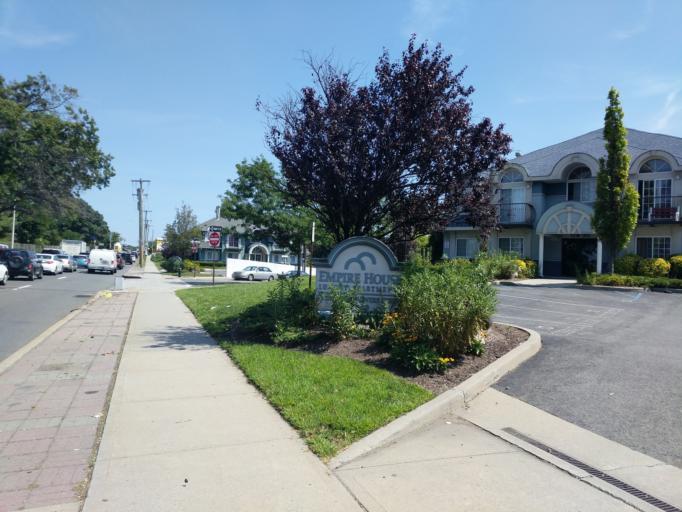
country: US
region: New York
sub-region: Queens County
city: Jamaica
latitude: 40.6670
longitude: -73.7734
